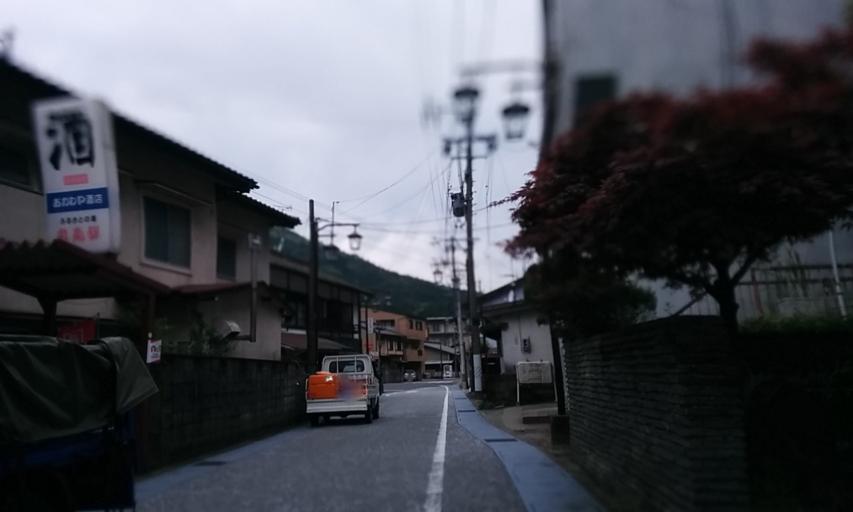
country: JP
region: Gifu
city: Gujo
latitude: 35.8126
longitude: 137.2382
